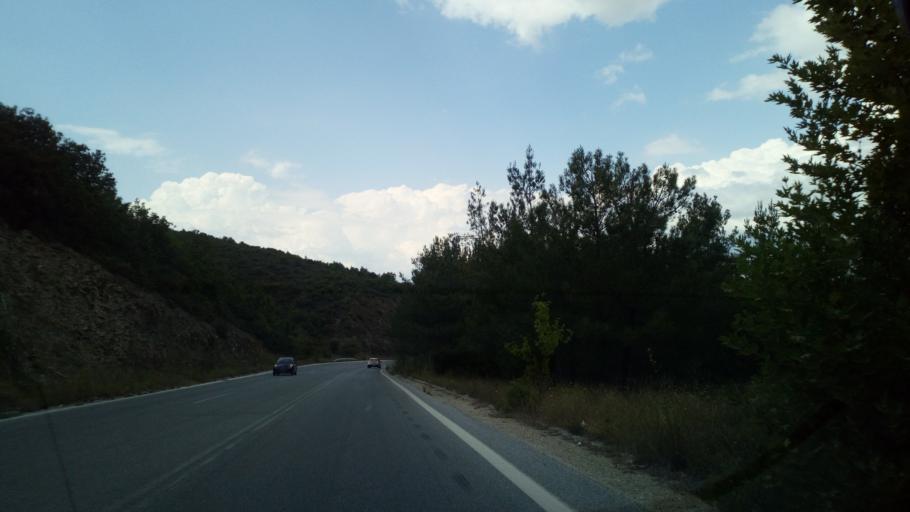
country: GR
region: Central Macedonia
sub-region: Nomos Chalkidikis
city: Polygyros
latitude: 40.4187
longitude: 23.4212
